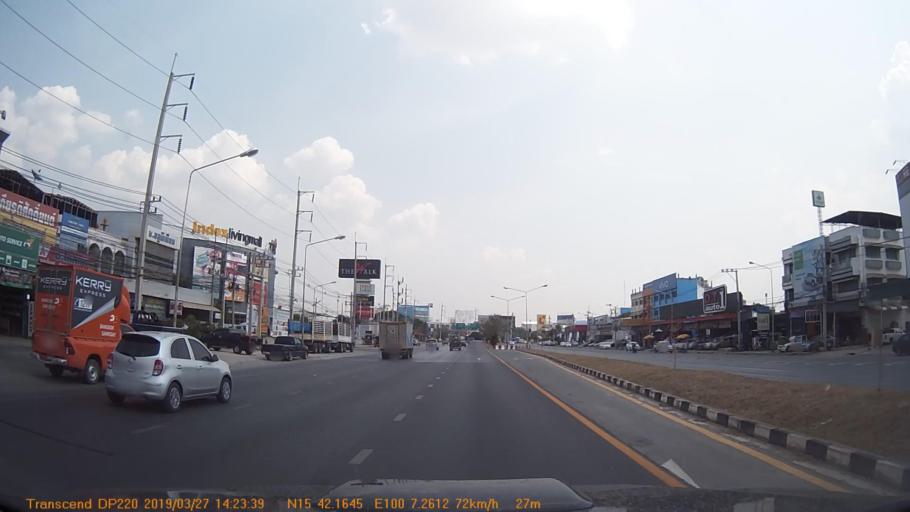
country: TH
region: Nakhon Sawan
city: Nakhon Sawan
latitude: 15.7025
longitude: 100.1211
